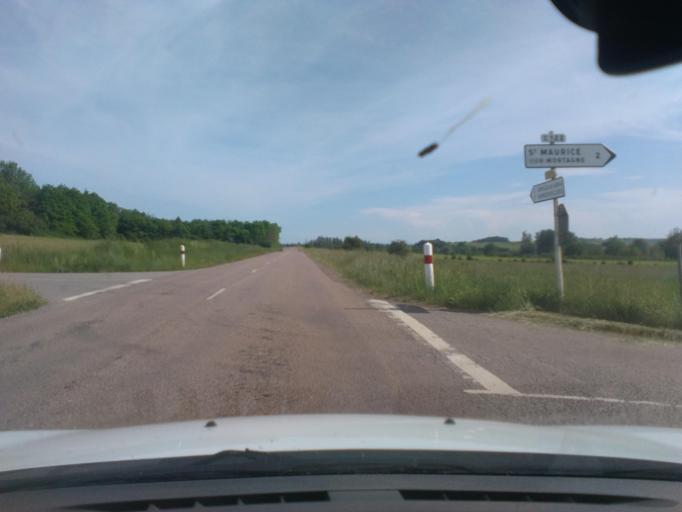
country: FR
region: Lorraine
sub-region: Departement des Vosges
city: Rambervillers
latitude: 48.4007
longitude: 6.5898
